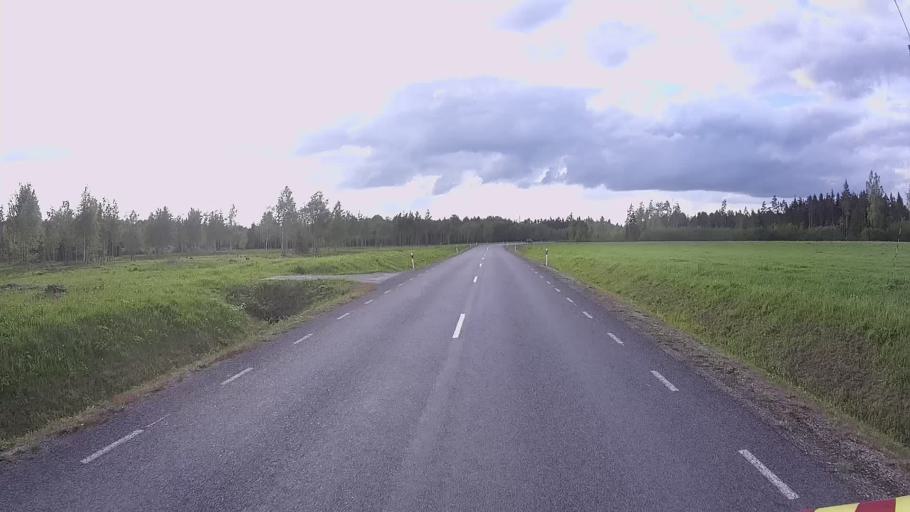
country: EE
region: Jogevamaa
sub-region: Mustvee linn
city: Mustvee
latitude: 59.0540
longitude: 27.0154
